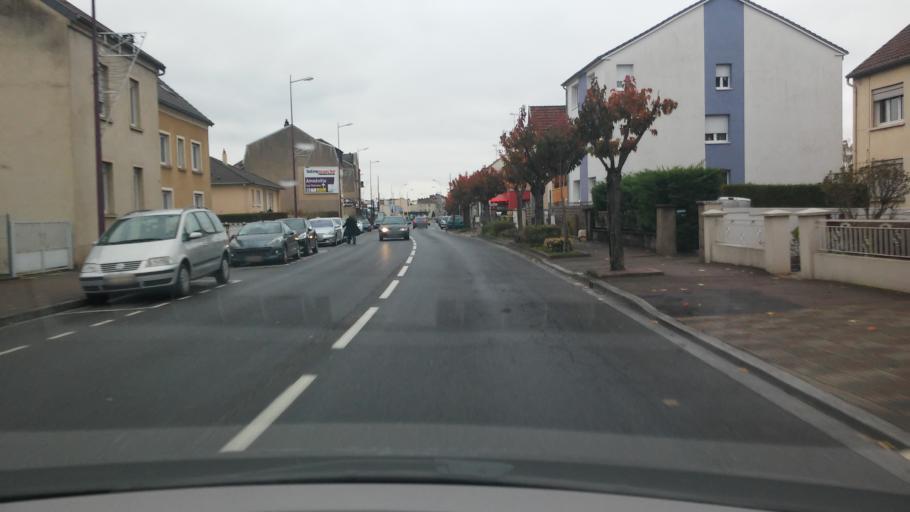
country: FR
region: Lorraine
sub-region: Departement de la Moselle
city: Talange
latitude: 49.2408
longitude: 6.1691
